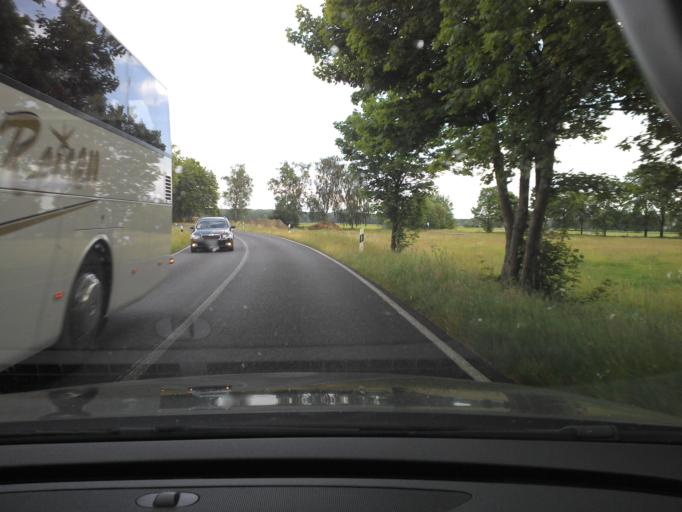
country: DE
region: Brandenburg
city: Burg
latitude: 51.8664
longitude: 14.1700
